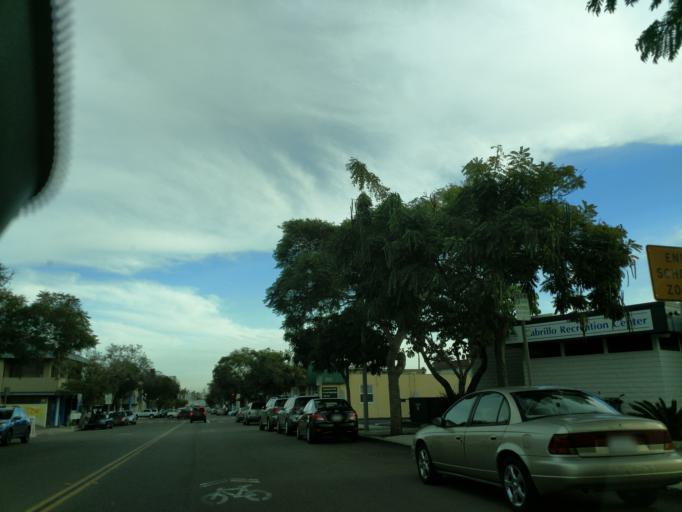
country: US
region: California
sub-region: San Diego County
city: Coronado
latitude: 32.7220
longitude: -117.2328
